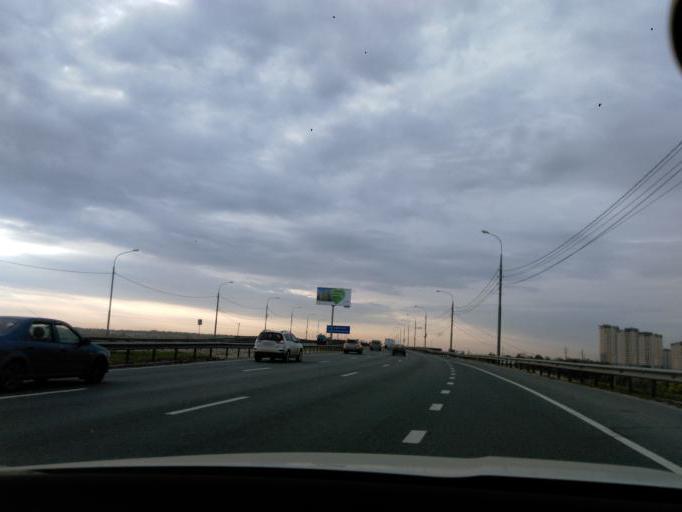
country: RU
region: Moskovskaya
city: Sheremet'yevskiy
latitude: 55.9745
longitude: 37.5250
